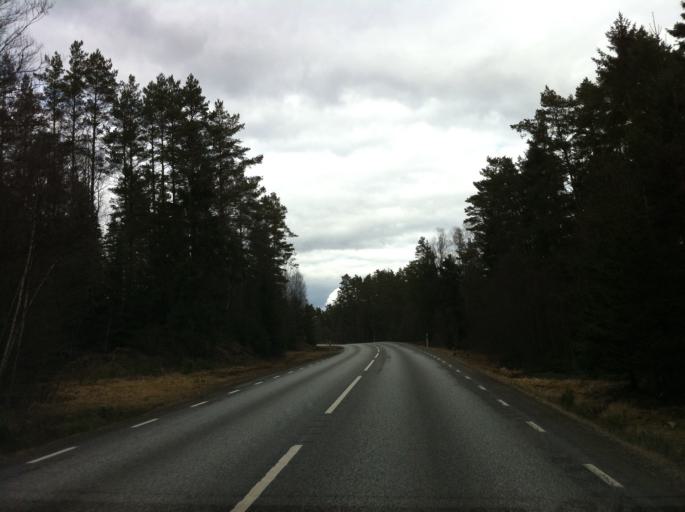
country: SE
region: Vaestra Goetaland
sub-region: Tranemo Kommun
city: Limmared
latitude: 57.5560
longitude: 13.4020
